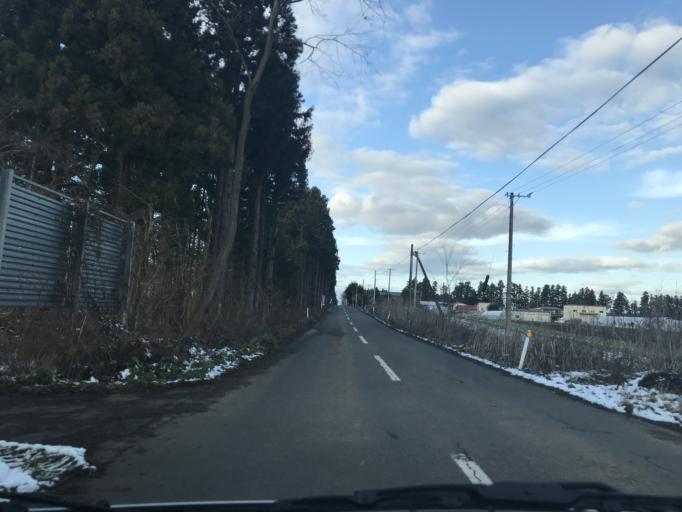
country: JP
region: Iwate
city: Kitakami
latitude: 39.2385
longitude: 141.0328
